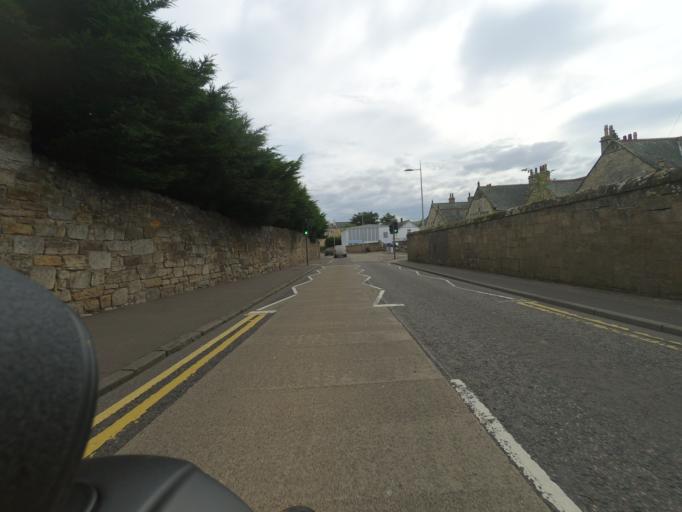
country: GB
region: Scotland
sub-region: Fife
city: Saint Andrews
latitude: 56.3374
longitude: -2.7890
